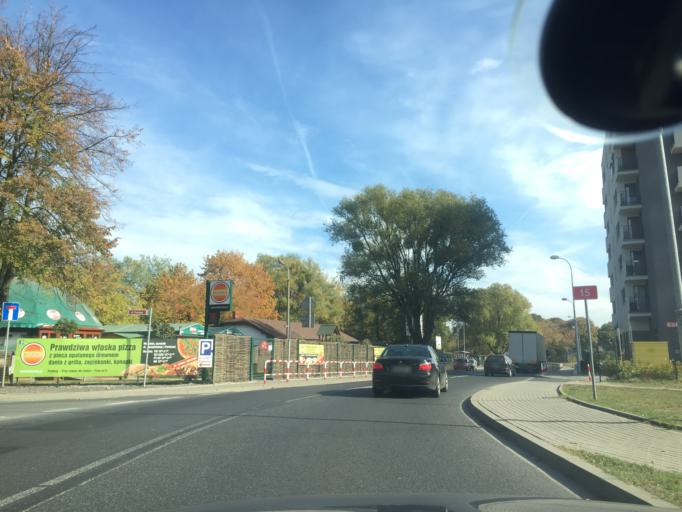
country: PL
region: Greater Poland Voivodeship
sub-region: Powiat wrzesinski
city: Wrzesnia
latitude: 52.3293
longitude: 17.5567
